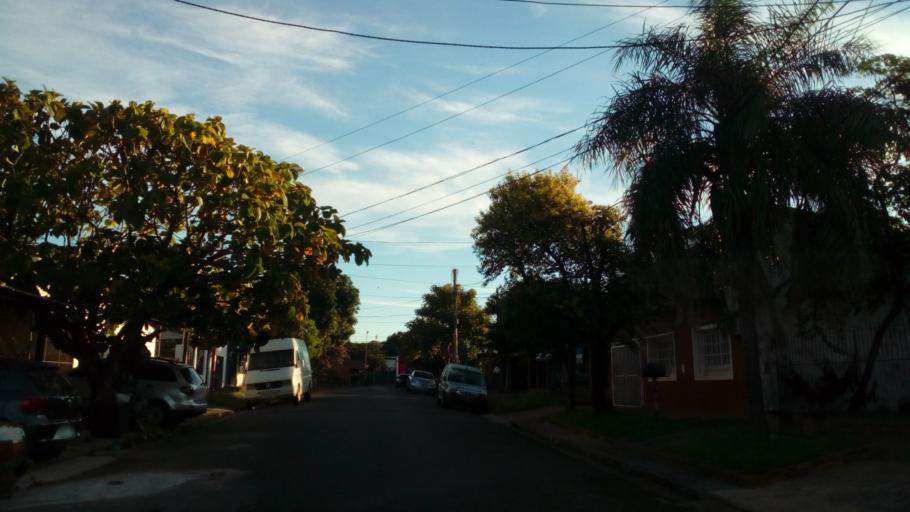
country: AR
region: Misiones
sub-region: Departamento de Capital
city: Posadas
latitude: -27.3684
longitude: -55.9115
